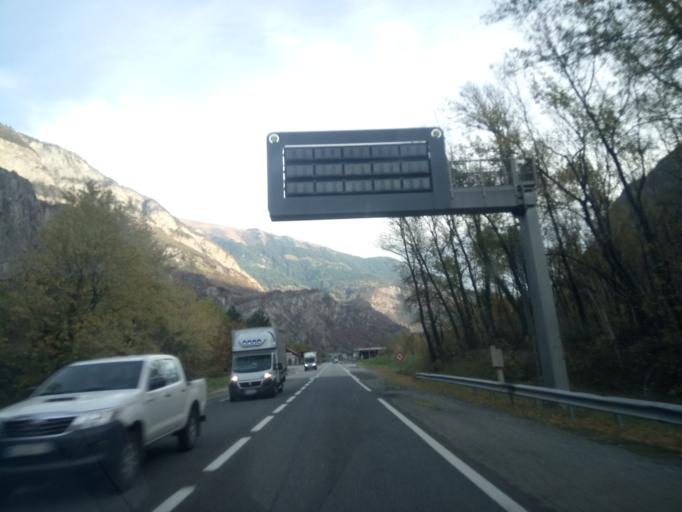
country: FR
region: Rhone-Alpes
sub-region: Departement de la Savoie
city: Saint-Jean-de-Maurienne
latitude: 45.3161
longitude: 6.3321
